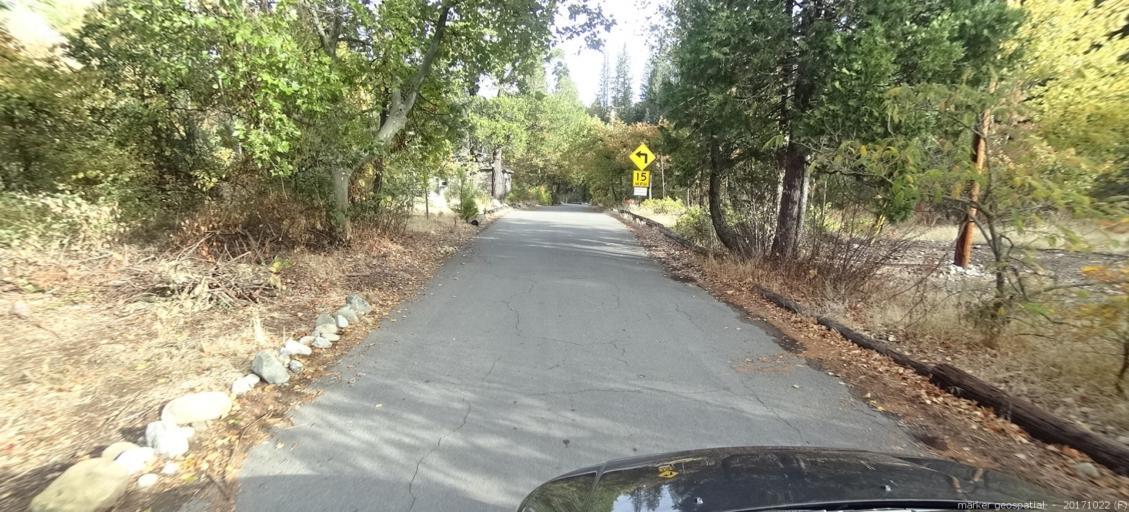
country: US
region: California
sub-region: Siskiyou County
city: Dunsmuir
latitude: 41.1437
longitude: -122.3145
